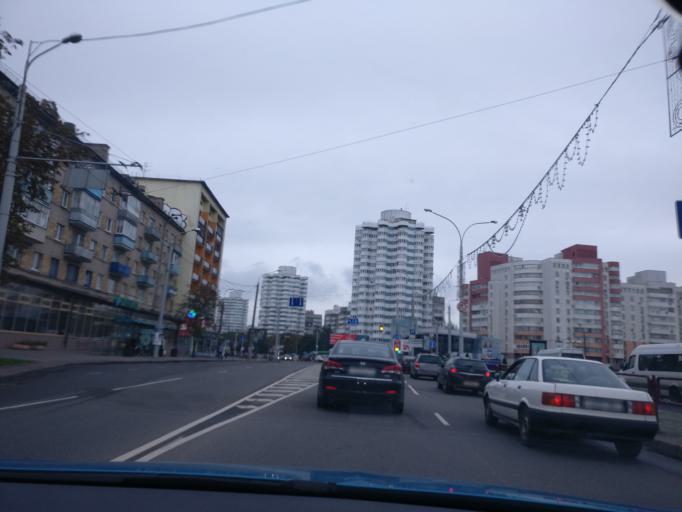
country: BY
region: Minsk
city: Minsk
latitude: 53.9188
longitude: 27.5767
